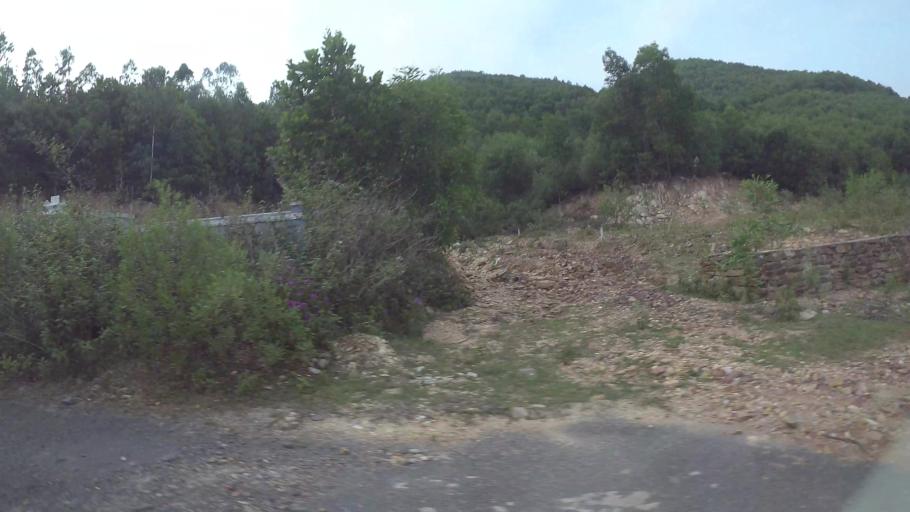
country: VN
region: Da Nang
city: Lien Chieu
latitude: 16.0622
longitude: 108.1159
